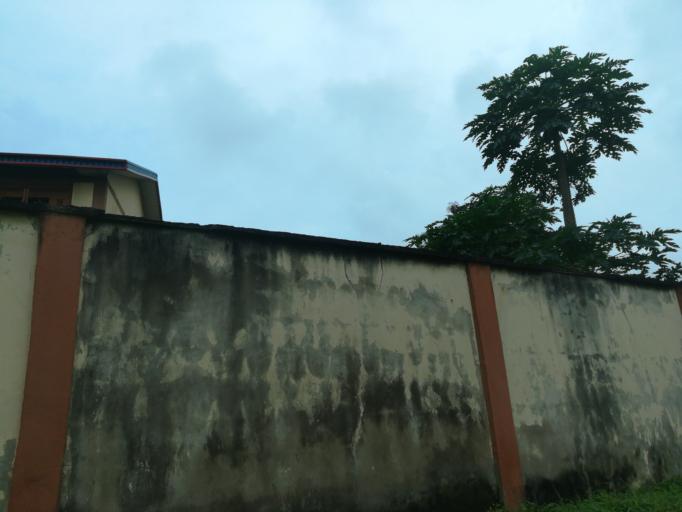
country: NG
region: Lagos
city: Oshodi
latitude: 6.5646
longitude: 3.3446
